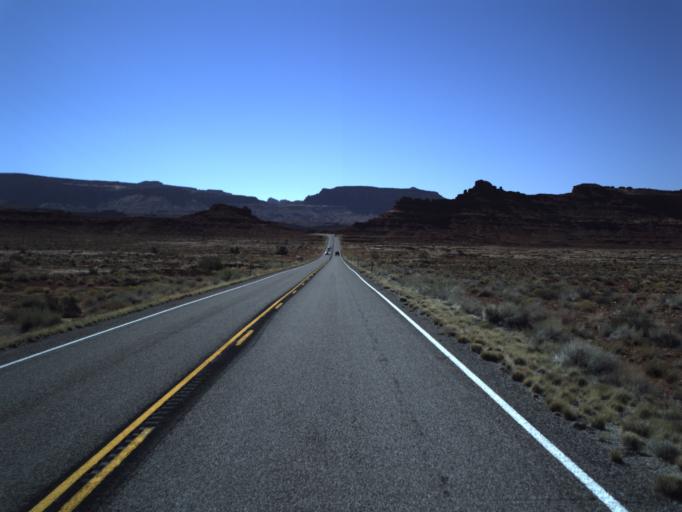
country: US
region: Utah
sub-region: San Juan County
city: Blanding
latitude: 37.8354
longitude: -110.3571
